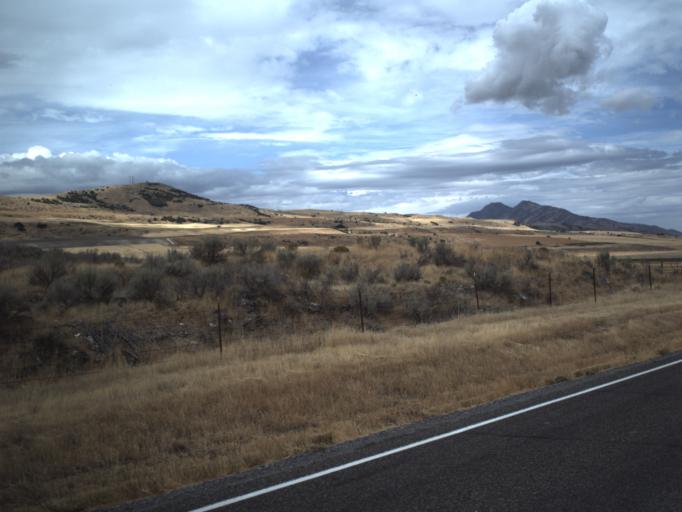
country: US
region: Utah
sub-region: Cache County
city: Benson
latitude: 41.8112
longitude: -111.9953
